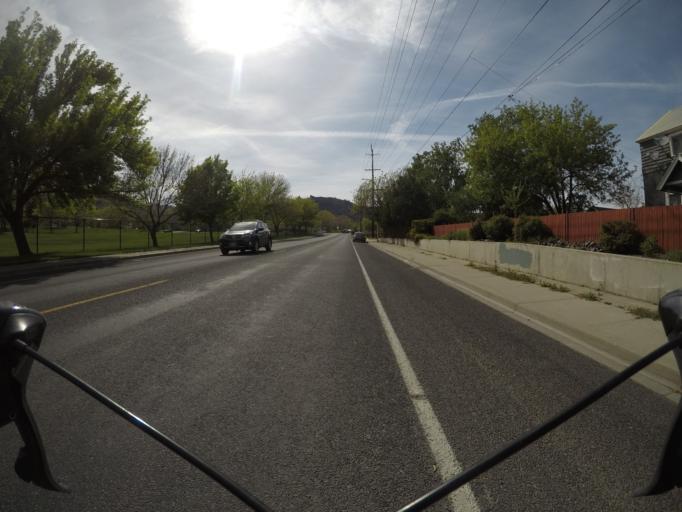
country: US
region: Washington
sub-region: Douglas County
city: East Wenatchee
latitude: 47.4043
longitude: -120.3063
